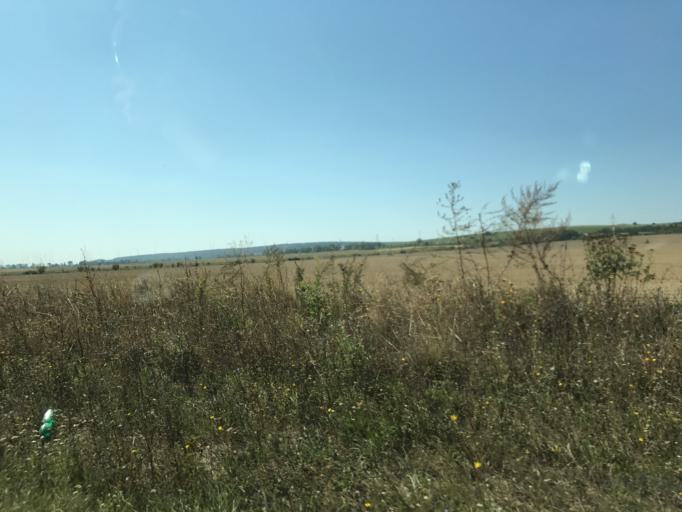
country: SK
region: Kosicky
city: Kosice
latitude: 48.6844
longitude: 21.2296
